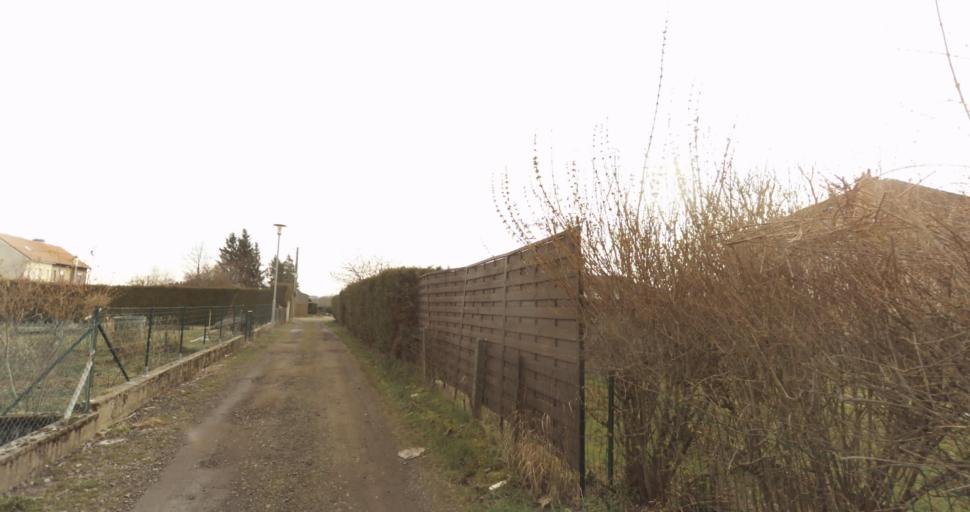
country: FR
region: Lorraine
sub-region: Departement de Meurthe-et-Moselle
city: Labry
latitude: 49.1645
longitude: 5.8787
